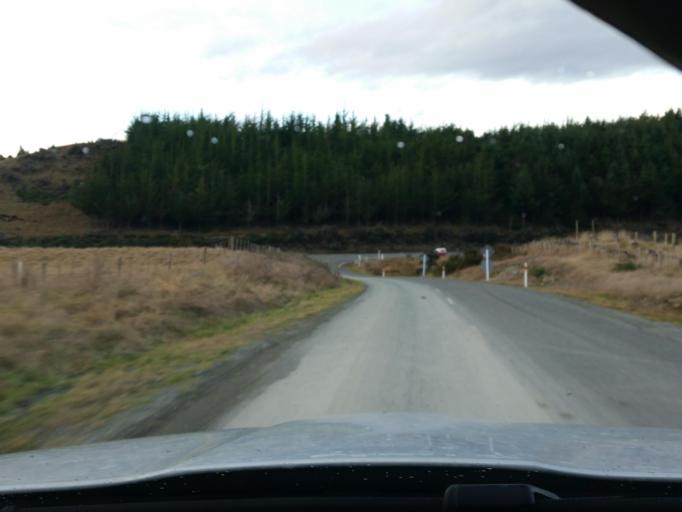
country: NZ
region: Southland
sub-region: Southland District
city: Te Anau
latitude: -45.4357
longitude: 167.7746
